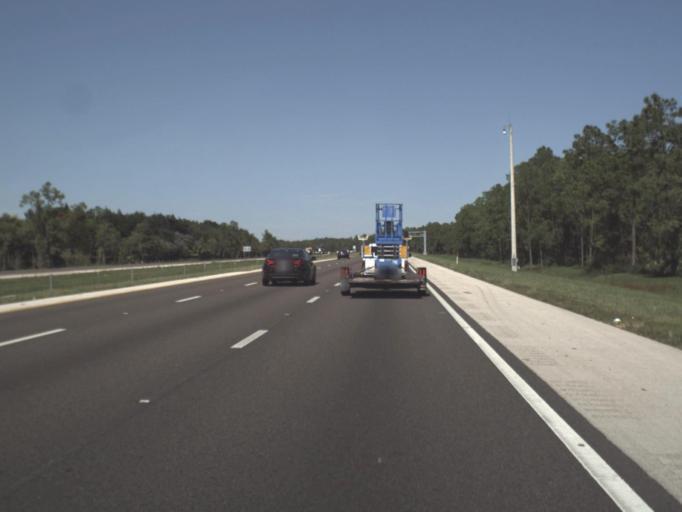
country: US
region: Florida
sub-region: Lee County
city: Bonita Springs
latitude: 26.3019
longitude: -81.7427
